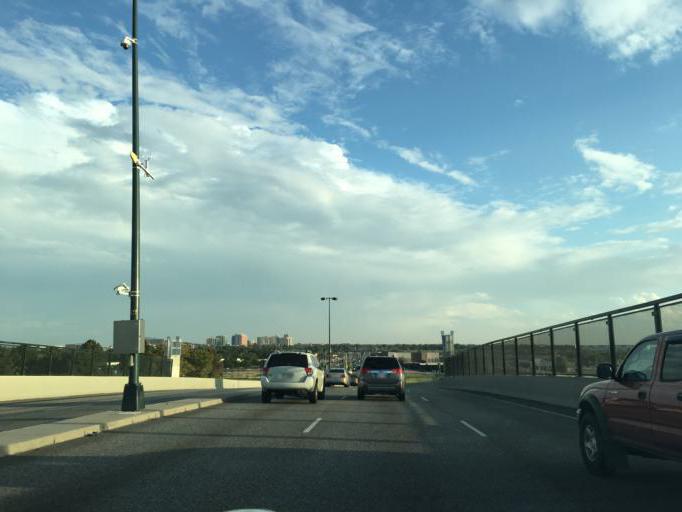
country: US
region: Colorado
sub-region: Adams County
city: Aurora
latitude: 39.7675
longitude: -104.8475
